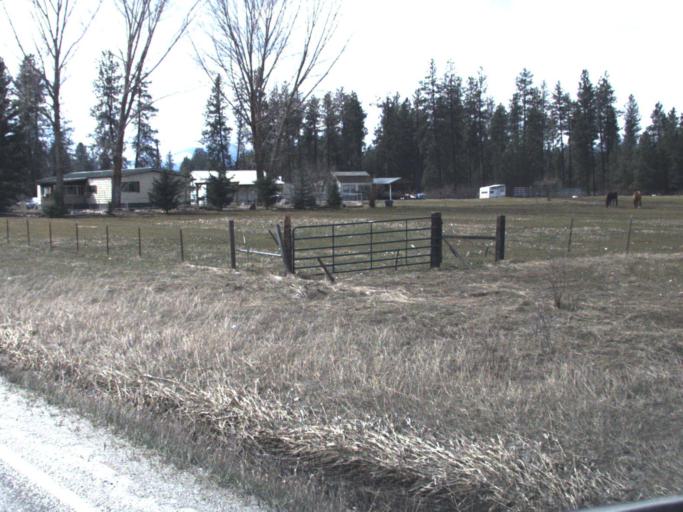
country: US
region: Washington
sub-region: Pend Oreille County
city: Newport
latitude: 48.3441
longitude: -117.3045
